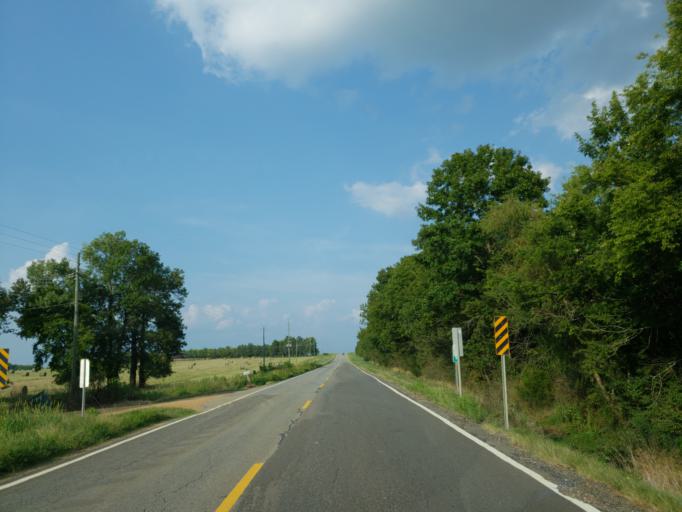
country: US
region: Alabama
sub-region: Greene County
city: Eutaw
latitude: 32.8019
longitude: -87.9590
